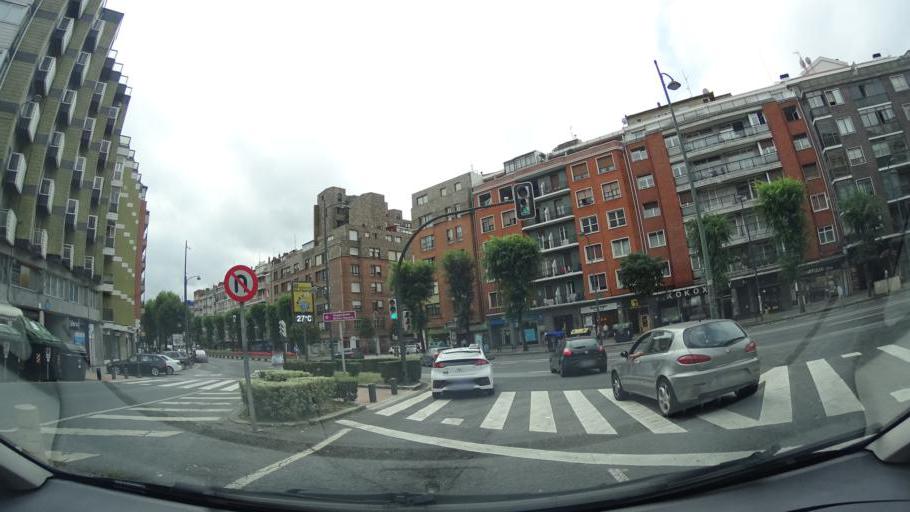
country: ES
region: Basque Country
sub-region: Bizkaia
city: Bilbao
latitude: 43.2722
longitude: -2.9480
